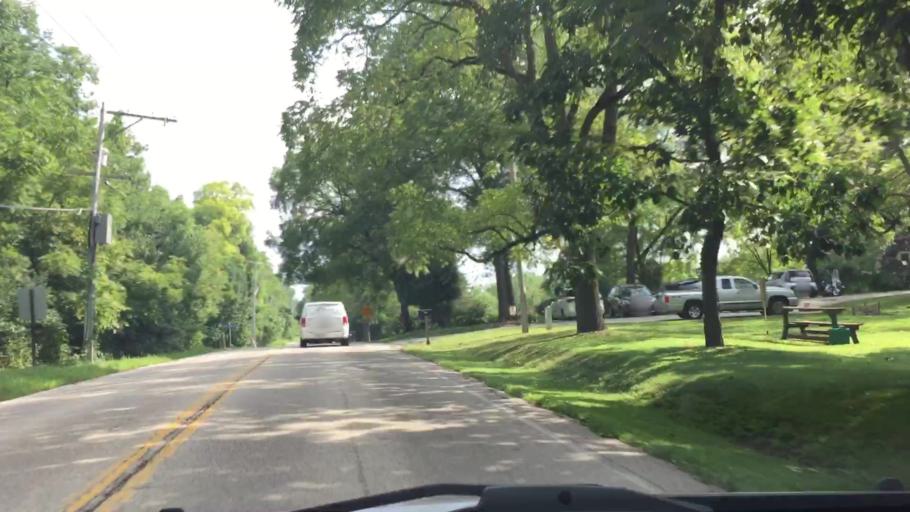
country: US
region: Wisconsin
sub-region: Waukesha County
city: Wales
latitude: 43.0430
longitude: -88.3496
